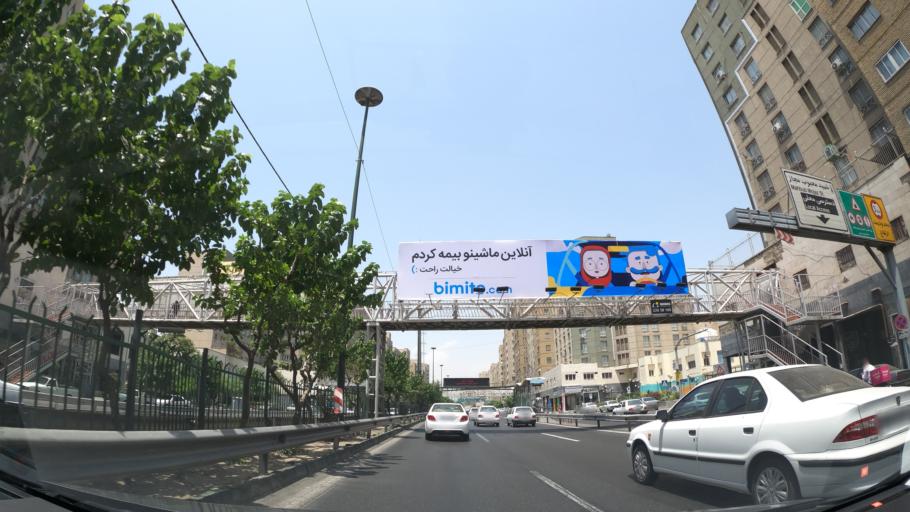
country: IR
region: Tehran
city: Tehran
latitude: 35.6827
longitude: 51.3801
